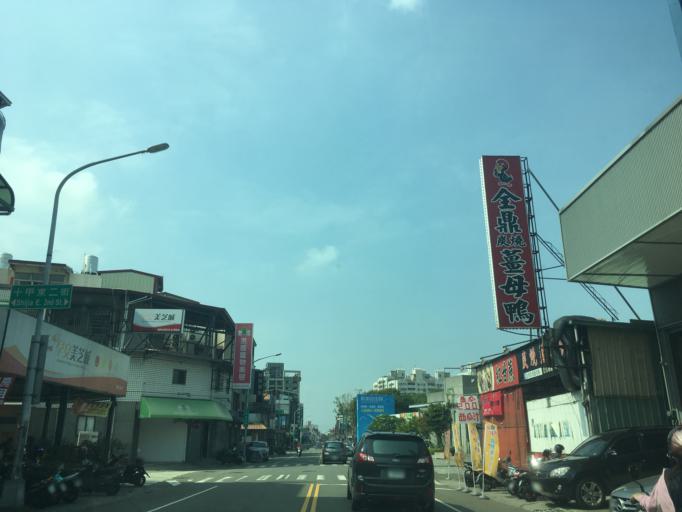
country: TW
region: Taiwan
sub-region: Taichung City
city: Taichung
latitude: 24.1478
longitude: 120.7101
